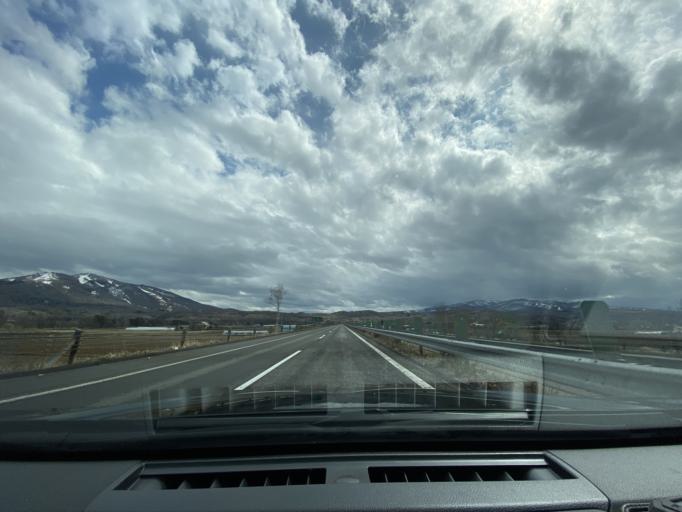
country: JP
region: Hokkaido
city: Fukagawa
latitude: 43.7291
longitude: 142.1653
